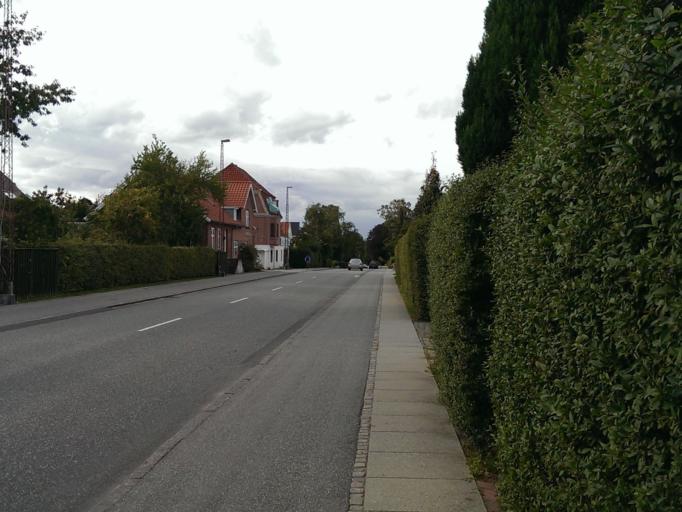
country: DK
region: Central Jutland
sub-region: Arhus Kommune
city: Arhus
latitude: 56.1326
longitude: 10.1806
